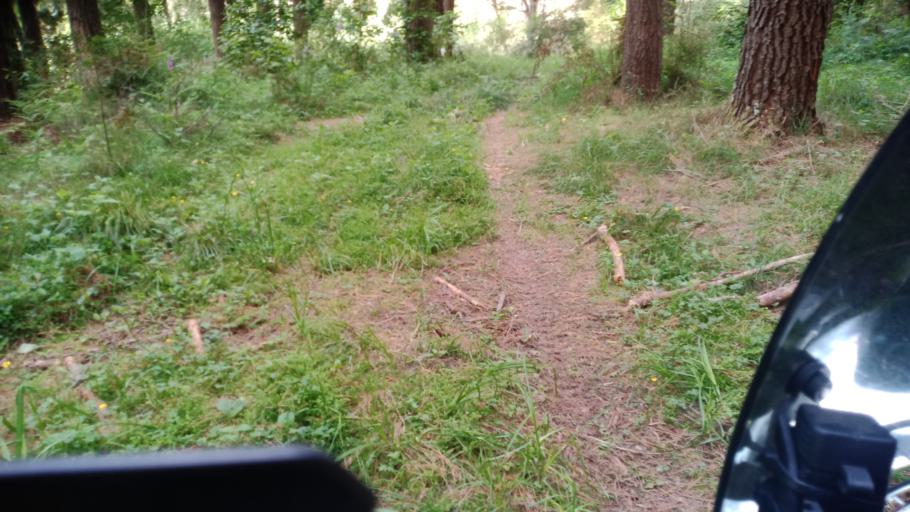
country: NZ
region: Gisborne
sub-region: Gisborne District
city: Gisborne
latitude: -38.4573
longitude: 177.9259
